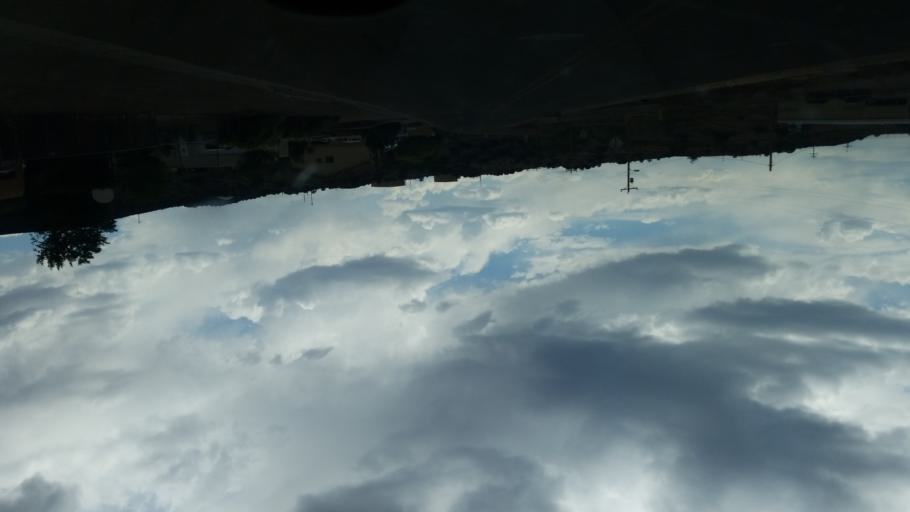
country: US
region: New Mexico
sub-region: Cibola County
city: Grants
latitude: 35.1613
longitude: -107.8458
